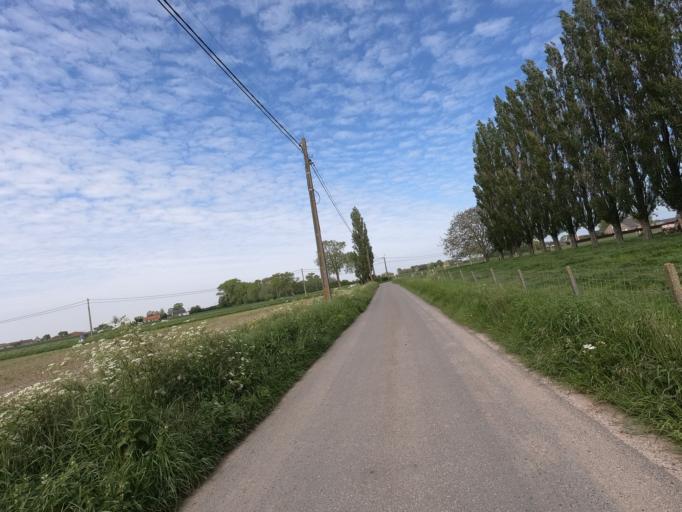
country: BE
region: Flanders
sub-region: Provincie West-Vlaanderen
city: Alveringem
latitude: 50.9659
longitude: 2.6817
